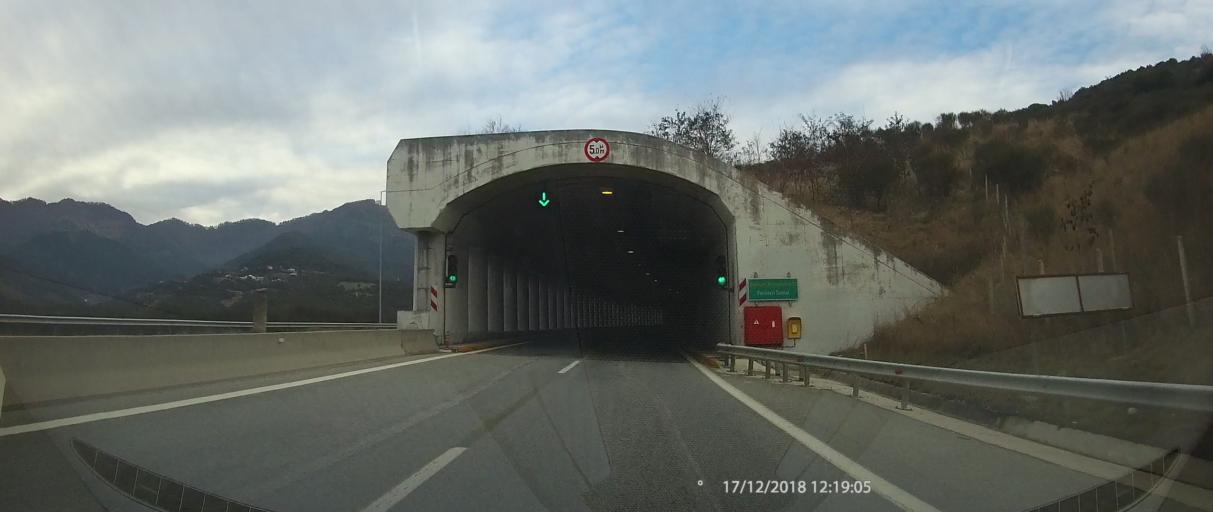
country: GR
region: Epirus
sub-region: Nomos Ioanninon
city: Metsovo
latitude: 39.7615
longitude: 21.0961
